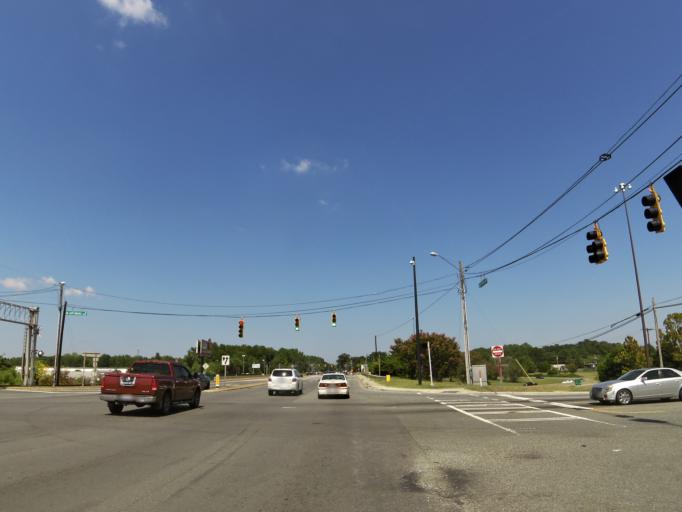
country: US
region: North Carolina
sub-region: Mecklenburg County
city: Charlotte
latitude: 35.2758
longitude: -80.8094
